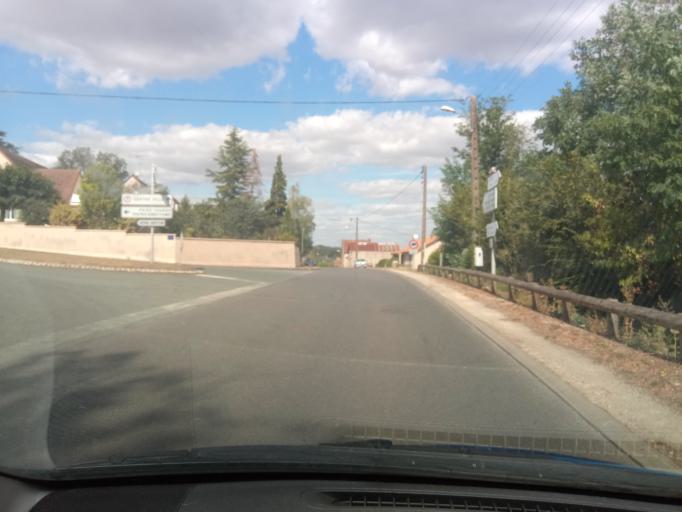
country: FR
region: Poitou-Charentes
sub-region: Departement de la Vienne
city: Saint-Savin
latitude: 46.5607
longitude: 0.8631
